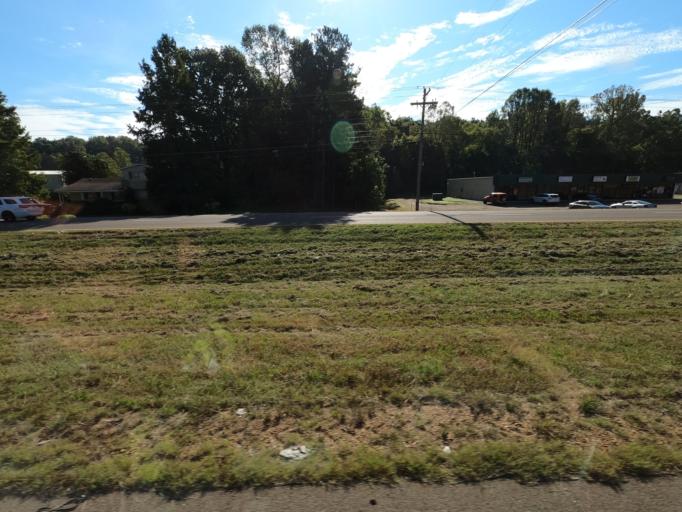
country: US
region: Tennessee
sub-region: Tipton County
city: Munford
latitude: 35.4258
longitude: -89.8131
